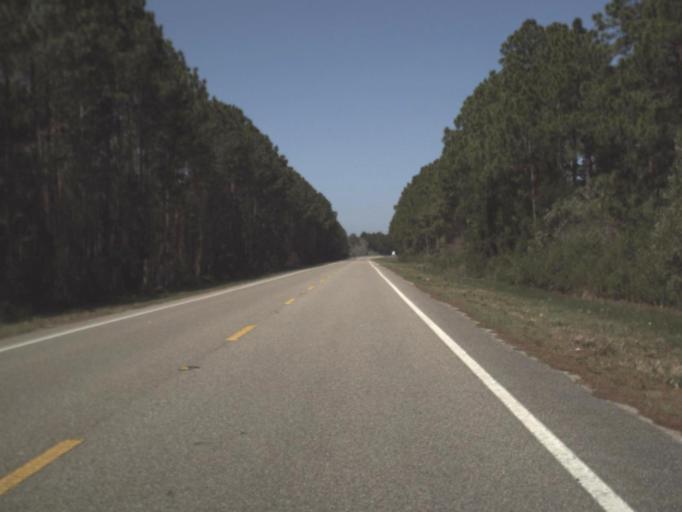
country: US
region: Florida
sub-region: Gulf County
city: Port Saint Joe
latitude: 29.7464
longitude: -85.2372
